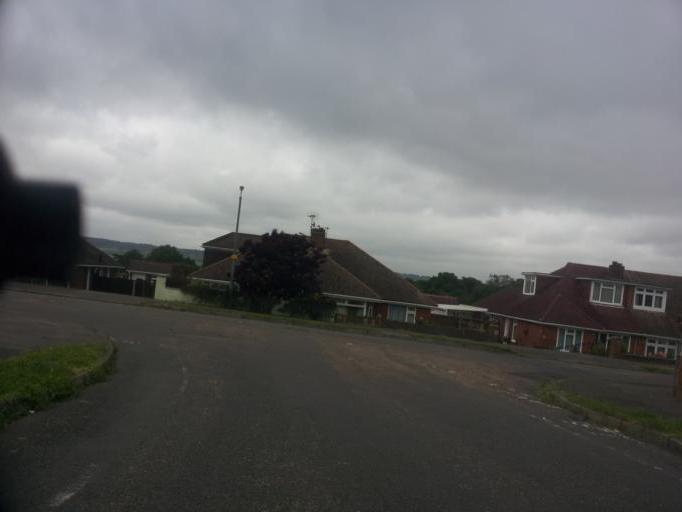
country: GB
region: England
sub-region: Kent
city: Maidstone
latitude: 51.2778
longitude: 0.4977
